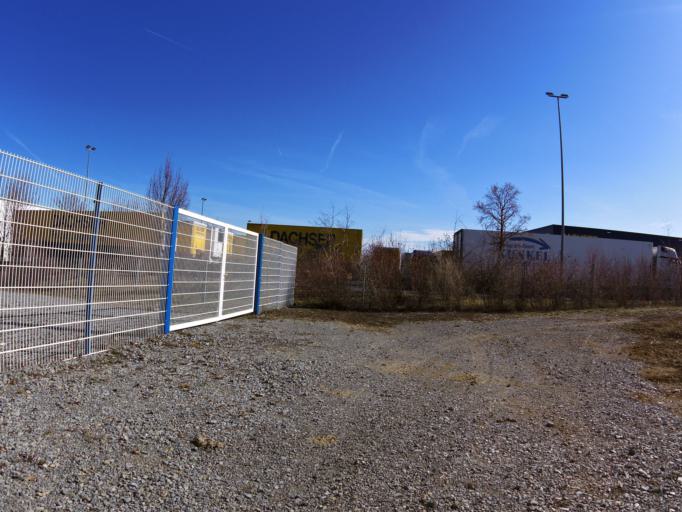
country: DE
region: Bavaria
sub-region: Regierungsbezirk Unterfranken
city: Kurnach
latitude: 49.8519
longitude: 10.0257
